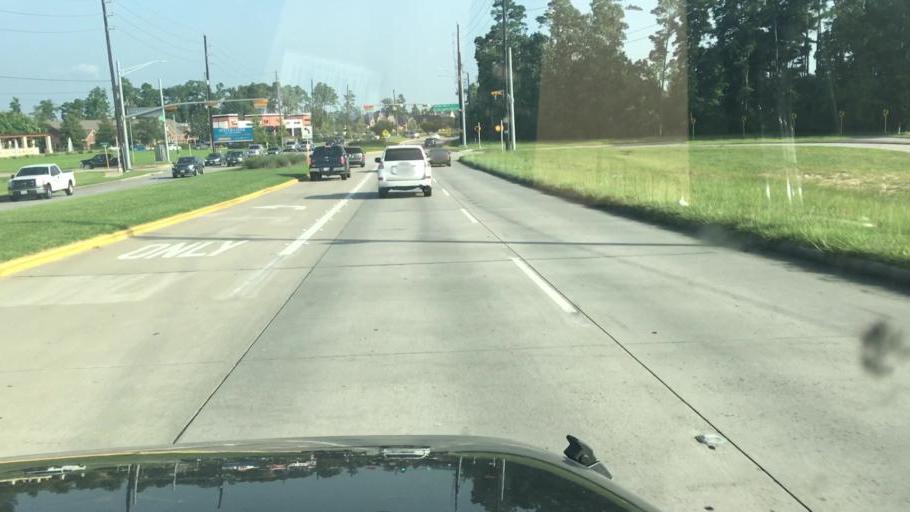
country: US
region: Texas
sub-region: Harris County
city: Atascocita
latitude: 29.9650
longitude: -95.1693
